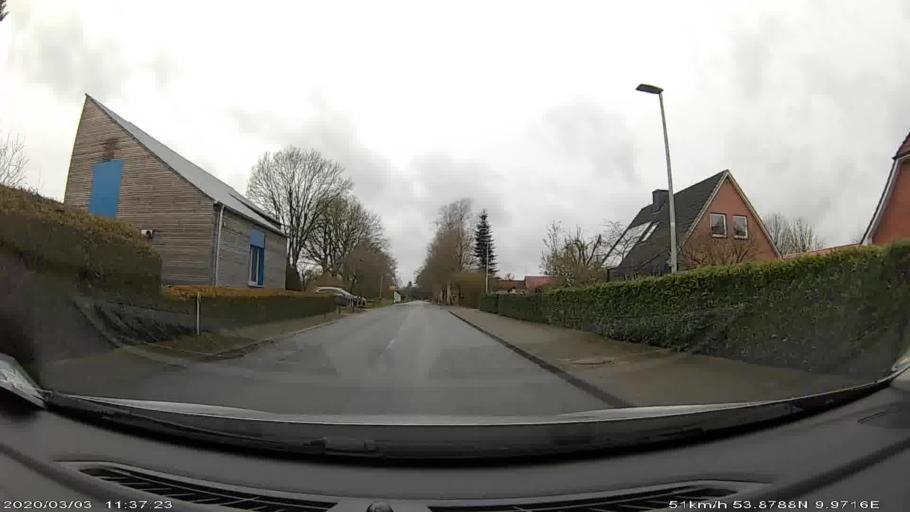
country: DE
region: Schleswig-Holstein
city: Schmalfeld
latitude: 53.8788
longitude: 9.9677
